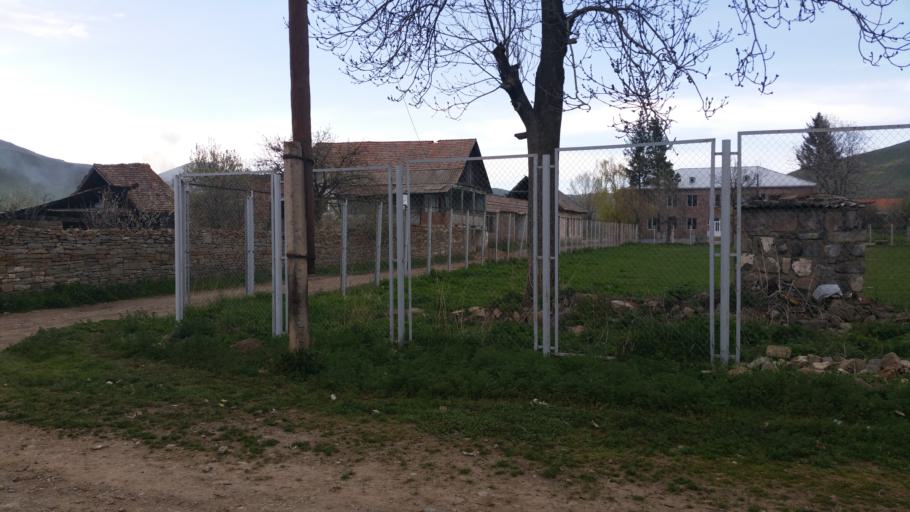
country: AM
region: Lorri
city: Urrut
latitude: 41.1451
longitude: 44.4453
